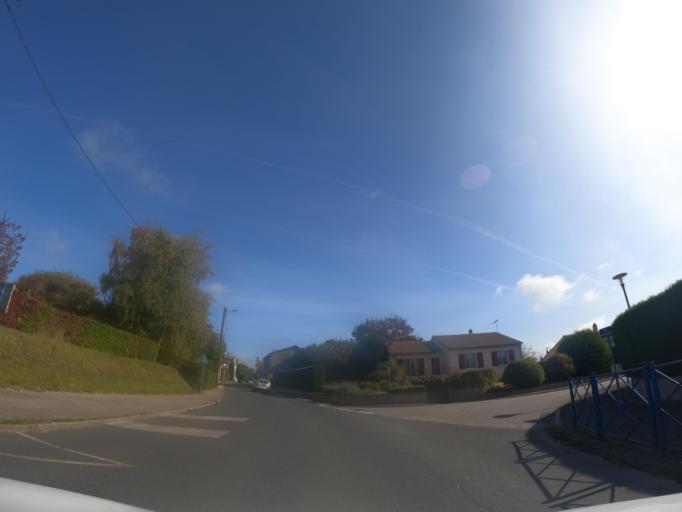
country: FR
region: Poitou-Charentes
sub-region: Departement des Deux-Sevres
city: Courlay
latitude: 46.7797
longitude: -0.5684
